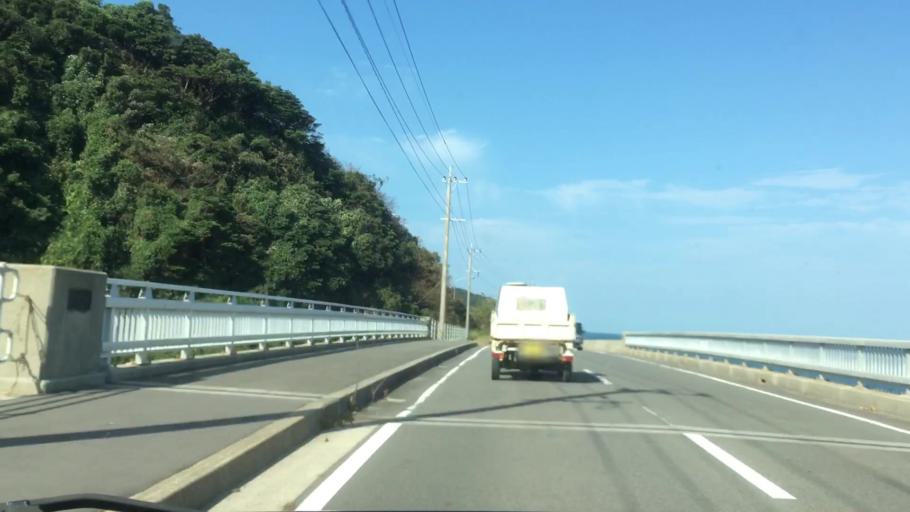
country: JP
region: Nagasaki
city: Sasebo
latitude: 33.0277
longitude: 129.5811
